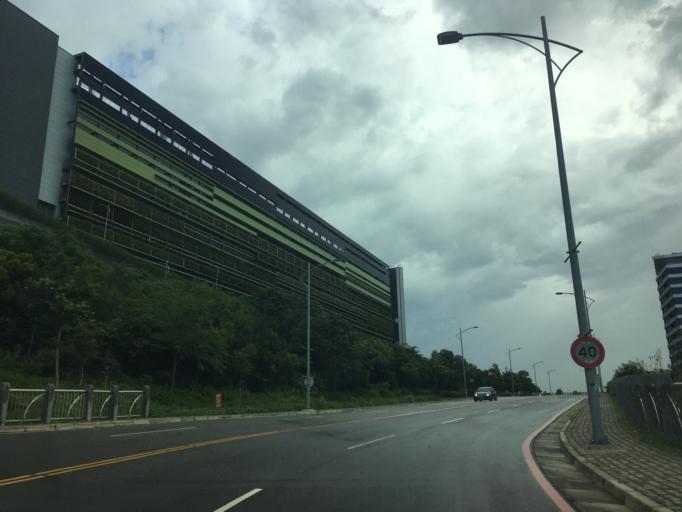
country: TW
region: Taiwan
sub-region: Taichung City
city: Taichung
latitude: 24.2071
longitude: 120.6102
